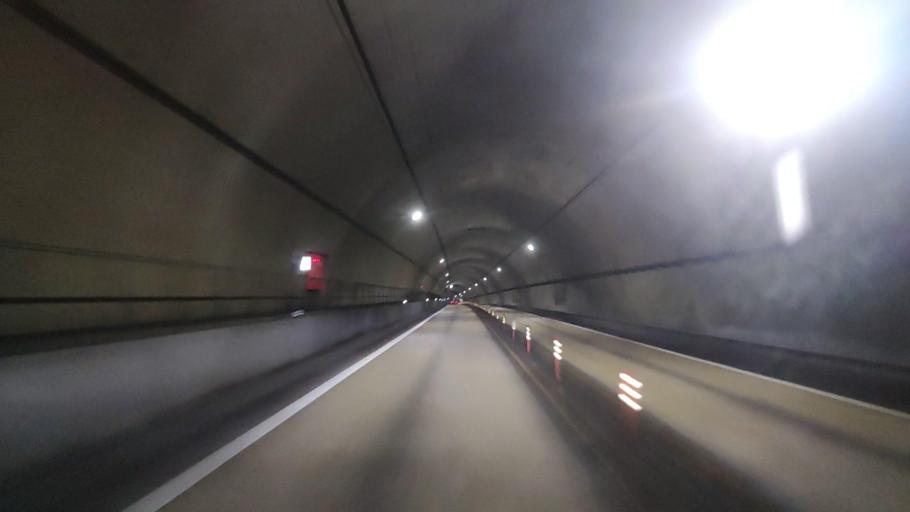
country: JP
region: Wakayama
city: Tanabe
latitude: 33.5710
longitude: 135.4820
